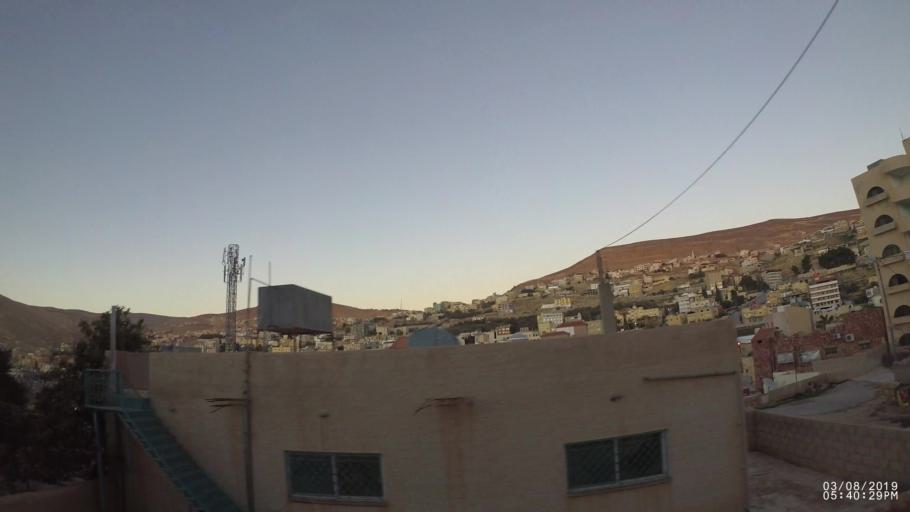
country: JO
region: Ma'an
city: Petra
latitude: 30.3194
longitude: 35.4768
